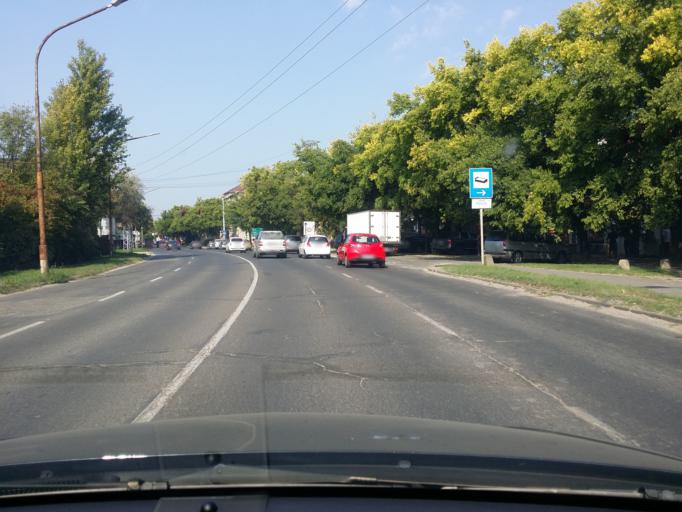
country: HU
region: Pest
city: Vac
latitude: 47.7764
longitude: 19.1371
